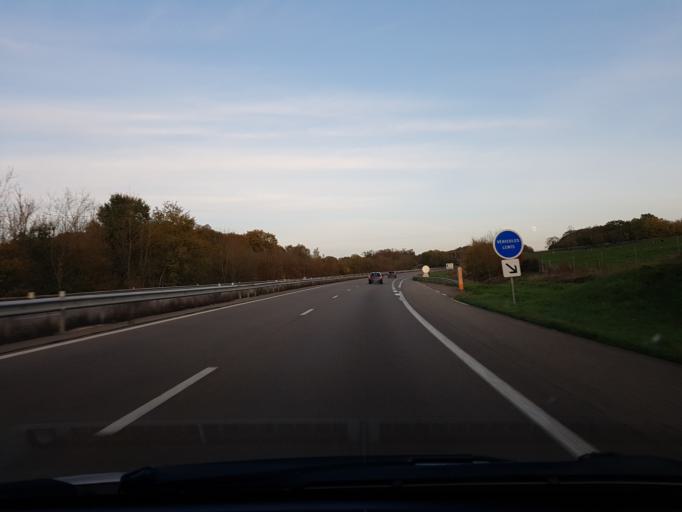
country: FR
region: Franche-Comte
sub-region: Departement du Doubs
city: Pirey
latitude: 47.2775
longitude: 5.9507
